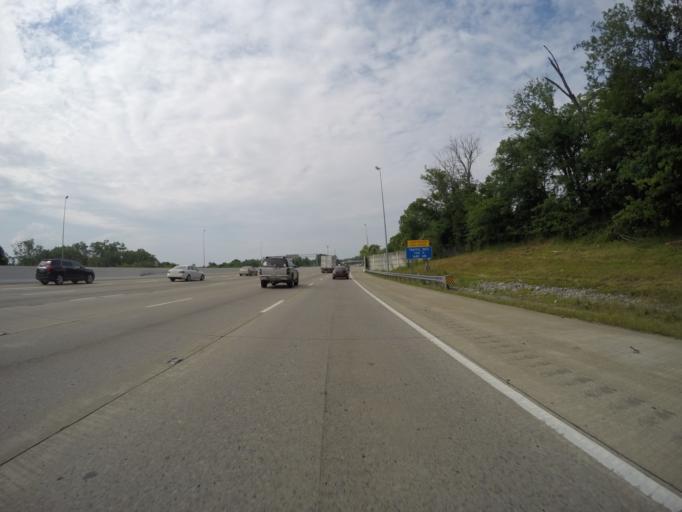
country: US
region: Tennessee
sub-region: Davidson County
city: Goodlettsville
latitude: 36.2542
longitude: -86.7391
